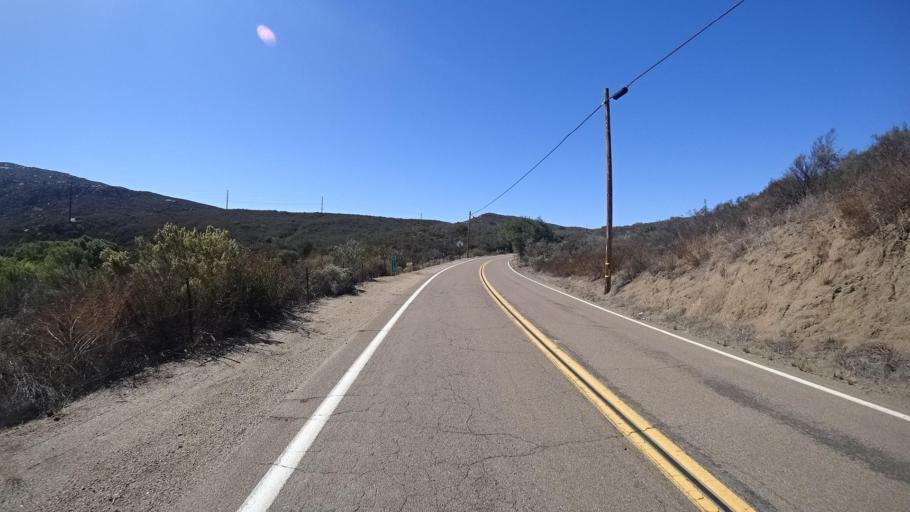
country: US
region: California
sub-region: San Diego County
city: Alpine
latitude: 32.7992
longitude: -116.7516
